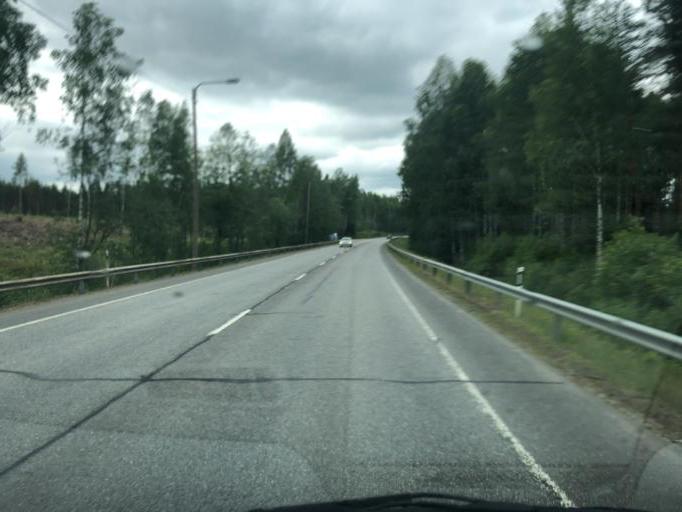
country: FI
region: Kymenlaakso
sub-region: Kouvola
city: Kouvola
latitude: 60.8976
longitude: 26.7478
